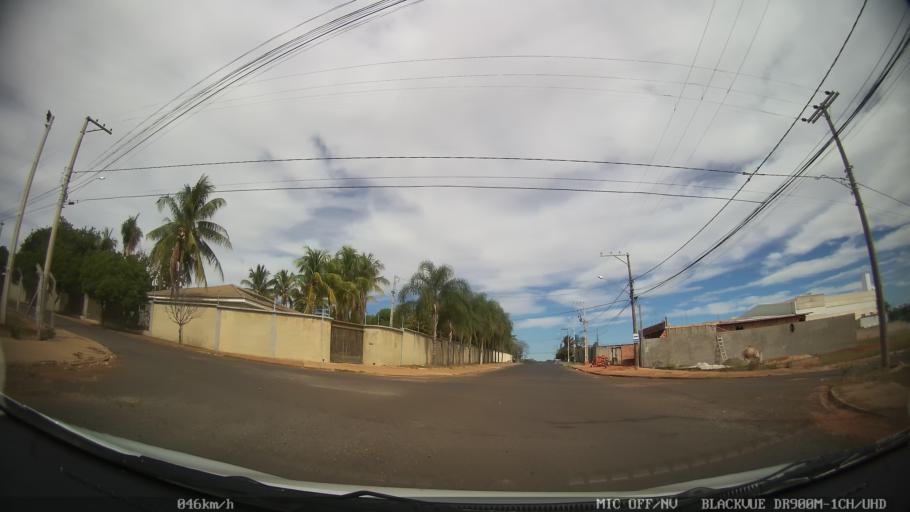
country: BR
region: Sao Paulo
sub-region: Catanduva
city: Catanduva
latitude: -21.1580
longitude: -48.9785
